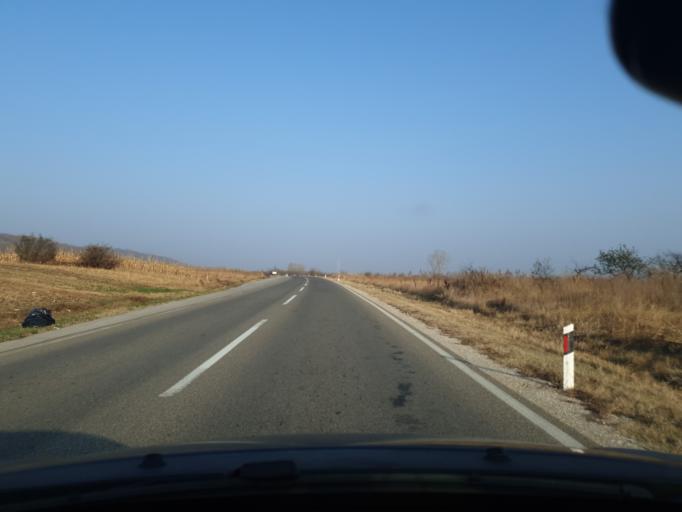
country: RS
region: Central Serbia
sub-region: Jablanicki Okrug
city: Leskovac
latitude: 42.9510
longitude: 21.9905
